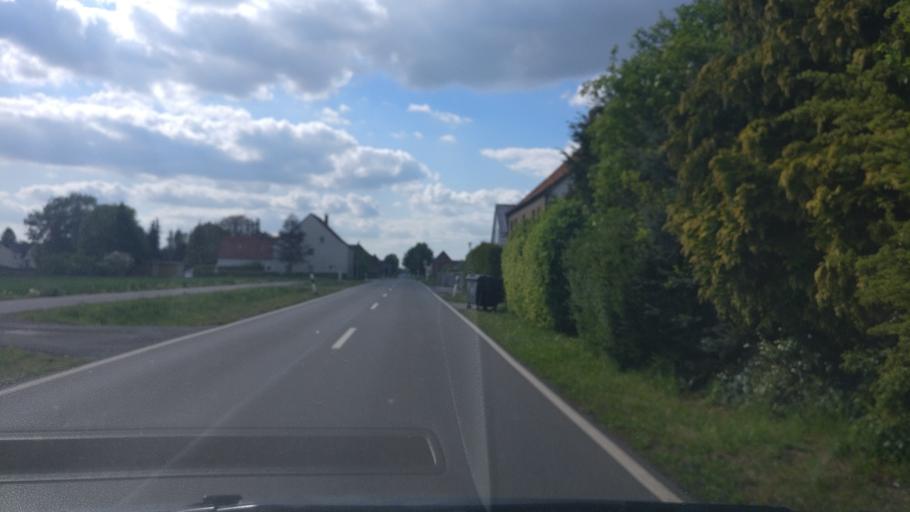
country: DE
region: North Rhine-Westphalia
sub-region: Regierungsbezirk Detmold
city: Leopoldshohe
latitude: 52.0068
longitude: 8.7116
